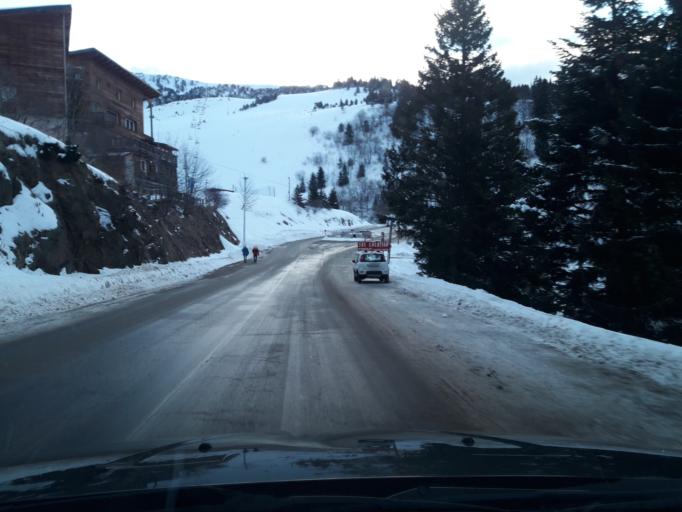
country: FR
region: Rhone-Alpes
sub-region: Departement de l'Isere
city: Vaulnaveys-le-Bas
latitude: 45.1251
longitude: 5.8762
